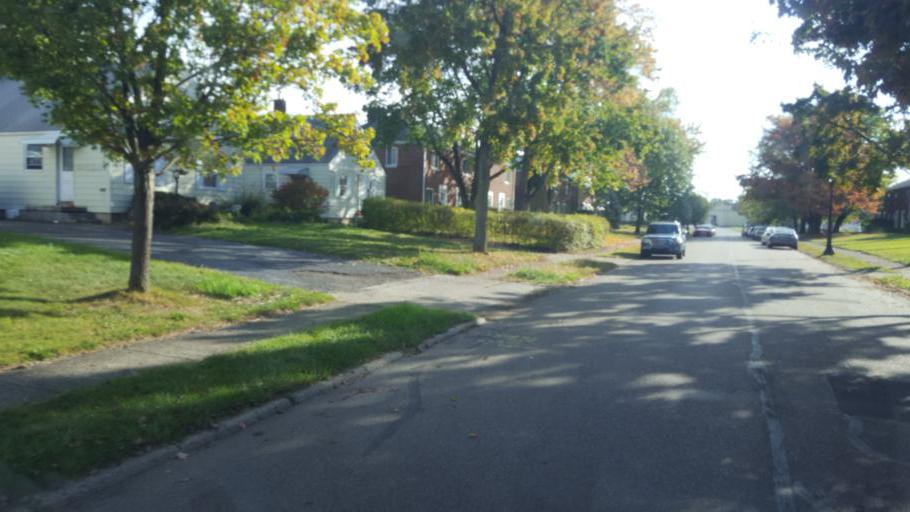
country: US
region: Ohio
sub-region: Franklin County
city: Worthington
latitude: 40.0413
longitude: -83.0024
